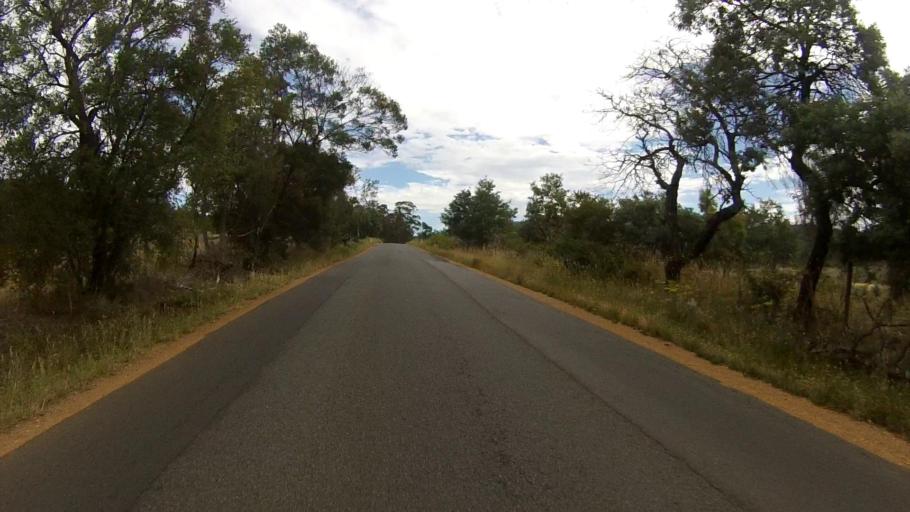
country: AU
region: Tasmania
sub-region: Clarence
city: Lindisfarne
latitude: -42.7531
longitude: 147.3778
